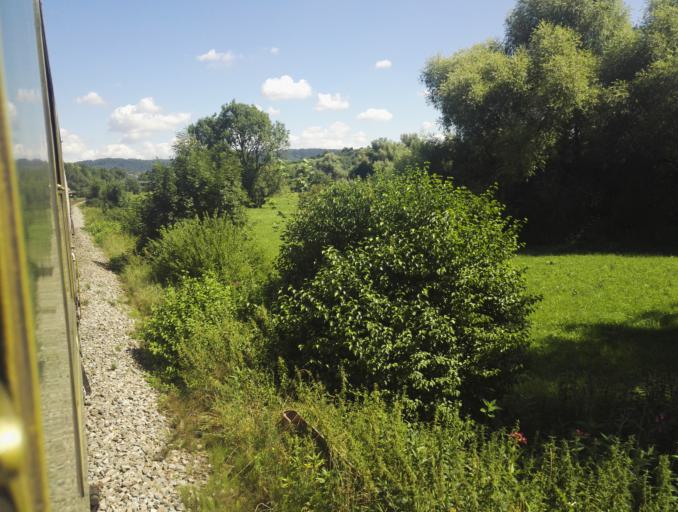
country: DE
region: Baden-Wuerttemberg
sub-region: Regierungsbezirk Stuttgart
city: Schorndorf
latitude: 48.8143
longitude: 9.5455
